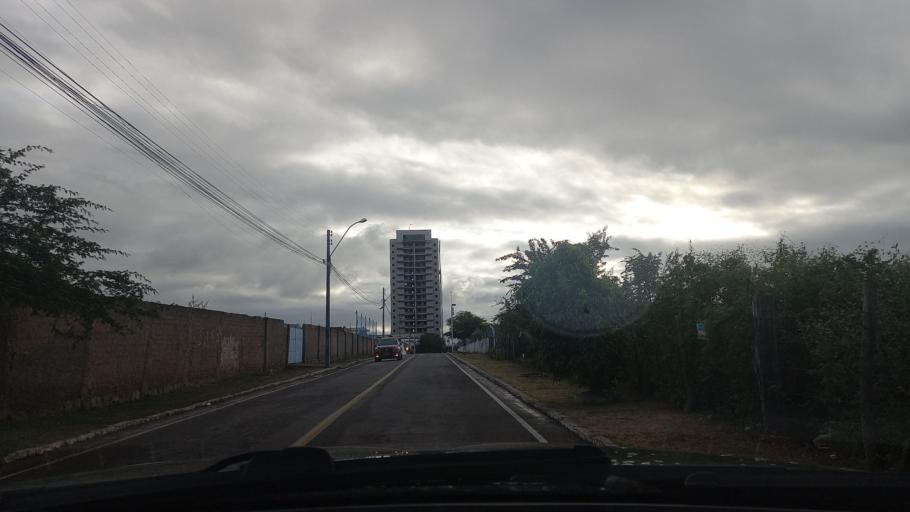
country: BR
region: Bahia
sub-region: Paulo Afonso
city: Paulo Afonso
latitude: -9.3977
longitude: -38.2297
